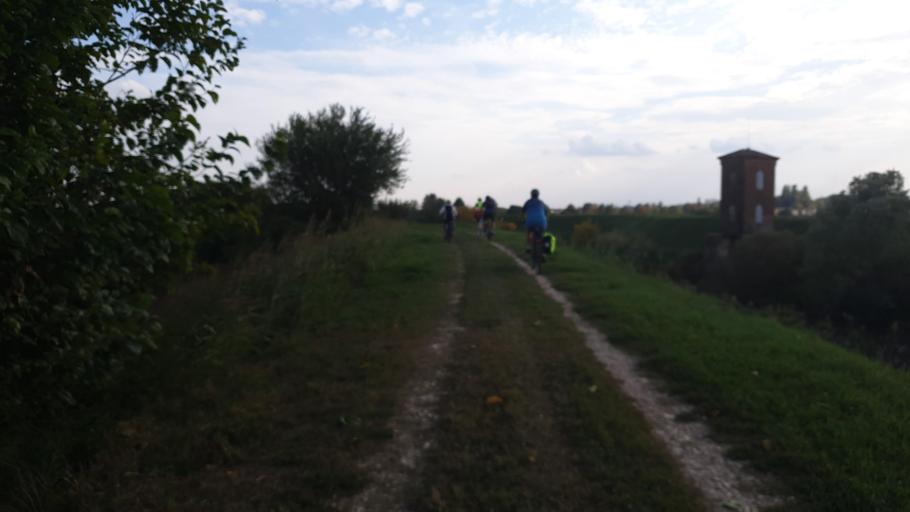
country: IT
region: Veneto
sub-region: Provincia di Padova
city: Montagnana
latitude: 45.2562
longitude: 11.4771
